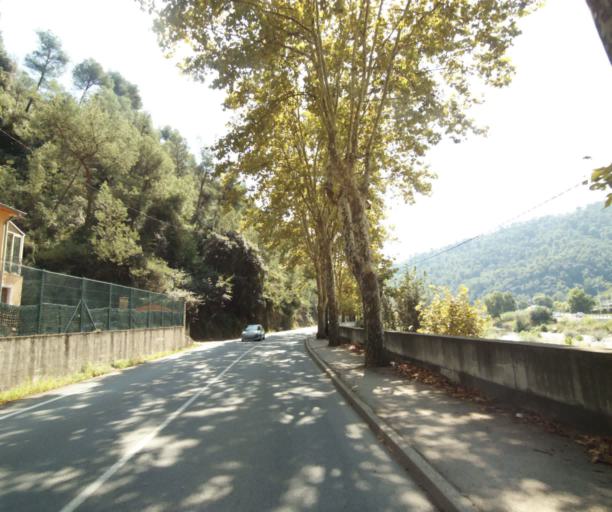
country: FR
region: Provence-Alpes-Cote d'Azur
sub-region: Departement des Alpes-Maritimes
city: Cantaron
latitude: 43.7633
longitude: 7.3220
